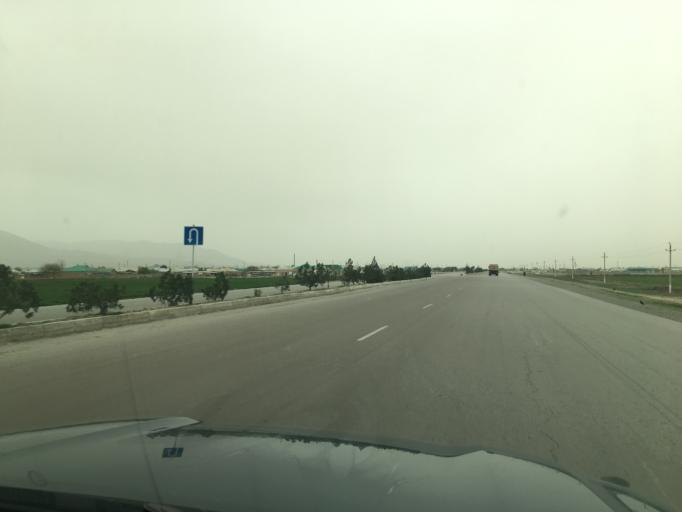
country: TM
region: Ahal
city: Baharly
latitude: 38.3927
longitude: 57.4835
